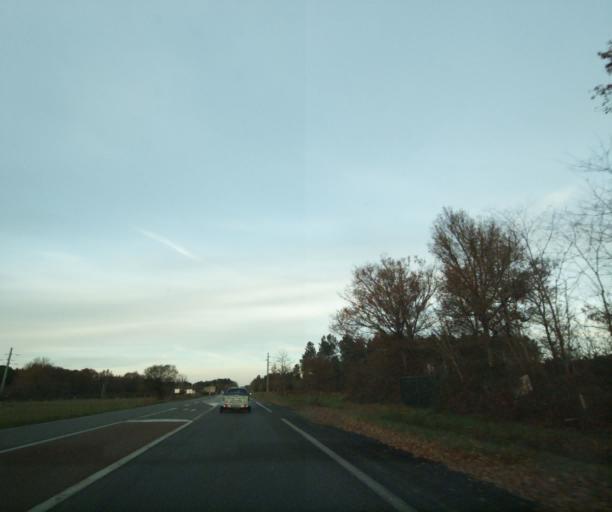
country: FR
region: Aquitaine
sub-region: Departement de la Gironde
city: Bazas
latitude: 44.4564
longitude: -0.2326
